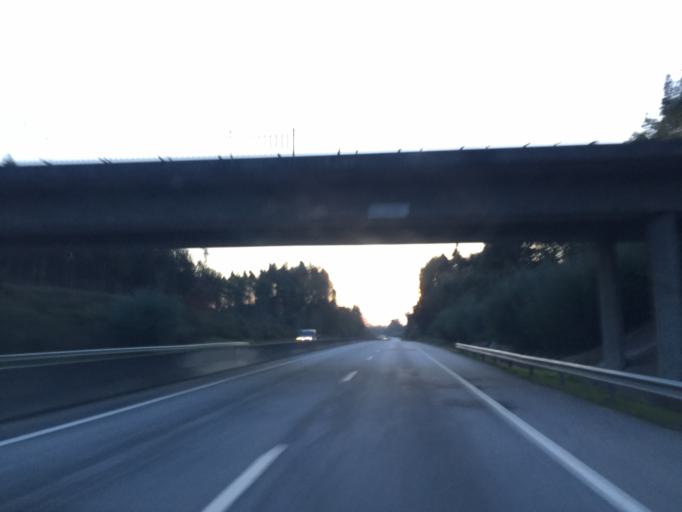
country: PT
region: Coimbra
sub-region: Tabua
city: Tabua
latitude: 40.4134
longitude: -8.0570
